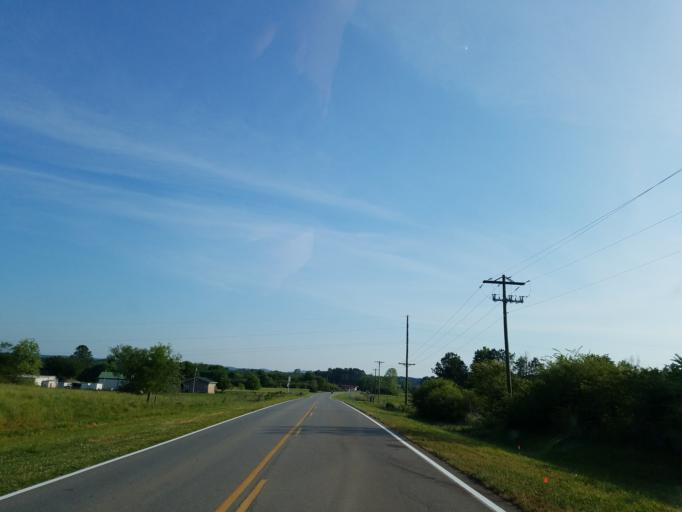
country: US
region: Georgia
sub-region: Chattooga County
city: Summerville
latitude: 34.4702
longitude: -85.2666
